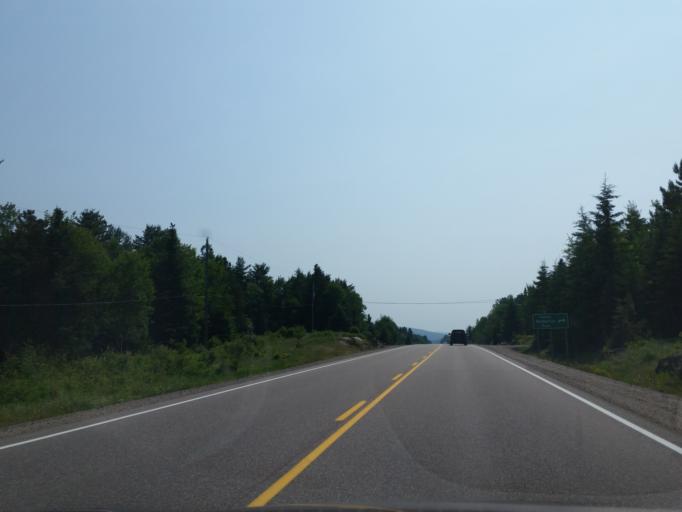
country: CA
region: Ontario
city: Mattawa
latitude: 46.3065
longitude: -78.6308
